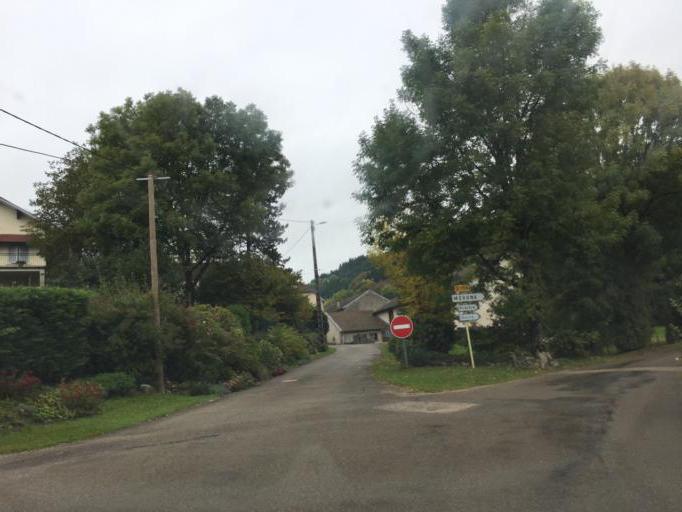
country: FR
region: Franche-Comte
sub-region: Departement du Jura
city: Orgelet
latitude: 46.5315
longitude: 5.6328
